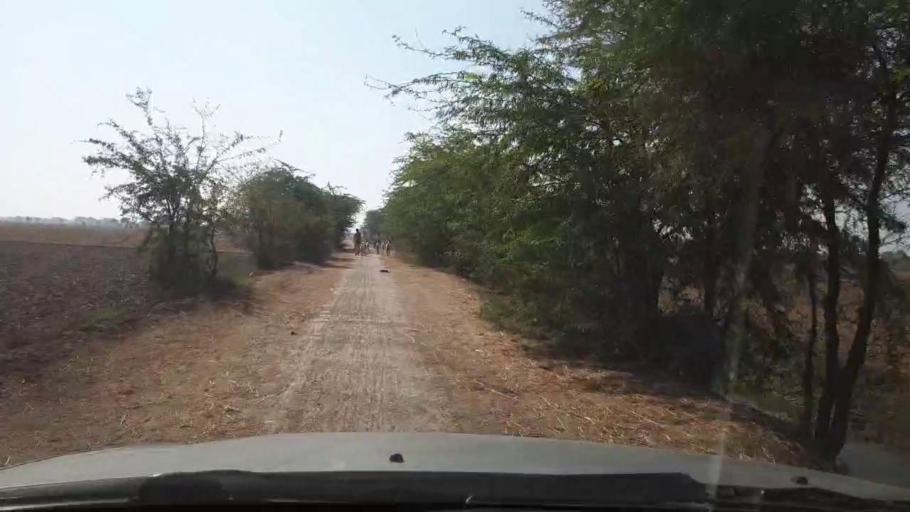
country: PK
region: Sindh
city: Kario
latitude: 24.8951
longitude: 68.5647
